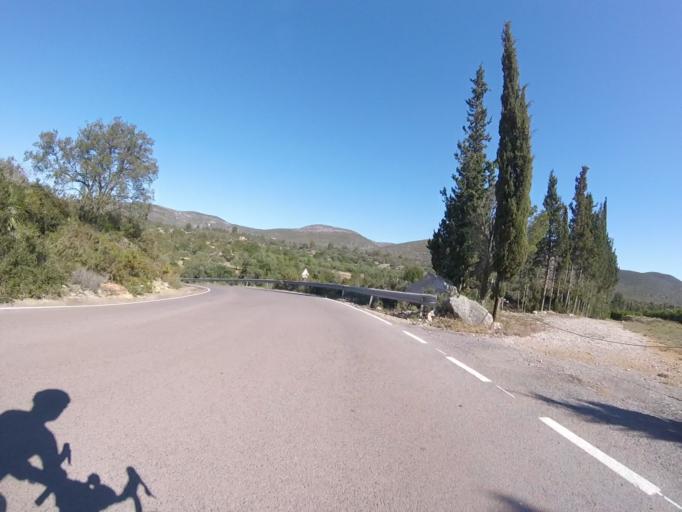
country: ES
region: Valencia
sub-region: Provincia de Castello
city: Santa Magdalena de Pulpis
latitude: 40.3705
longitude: 0.2744
